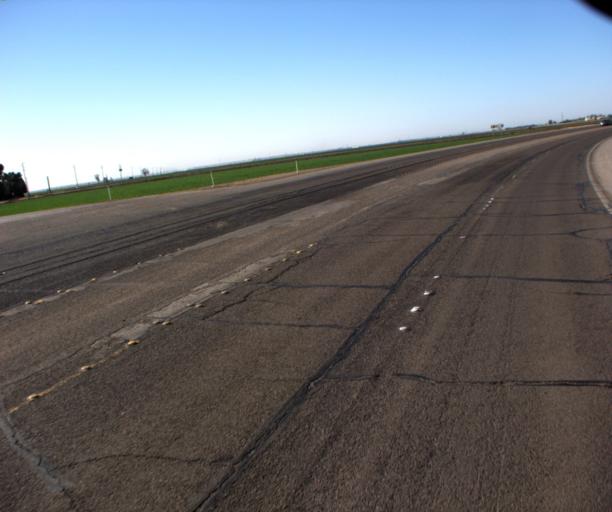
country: US
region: Arizona
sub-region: Yuma County
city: Somerton
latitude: 32.5694
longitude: -114.7705
